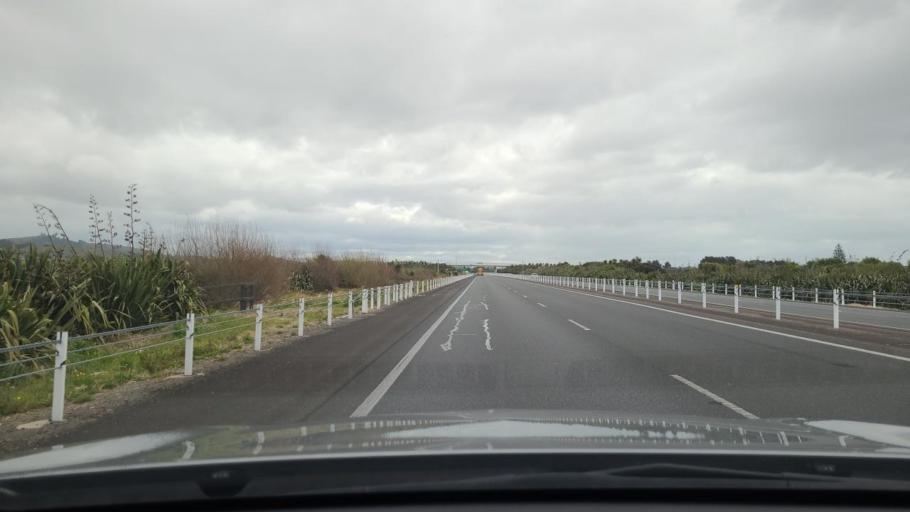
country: NZ
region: Bay of Plenty
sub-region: Western Bay of Plenty District
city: Maketu
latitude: -37.7218
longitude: 176.3135
